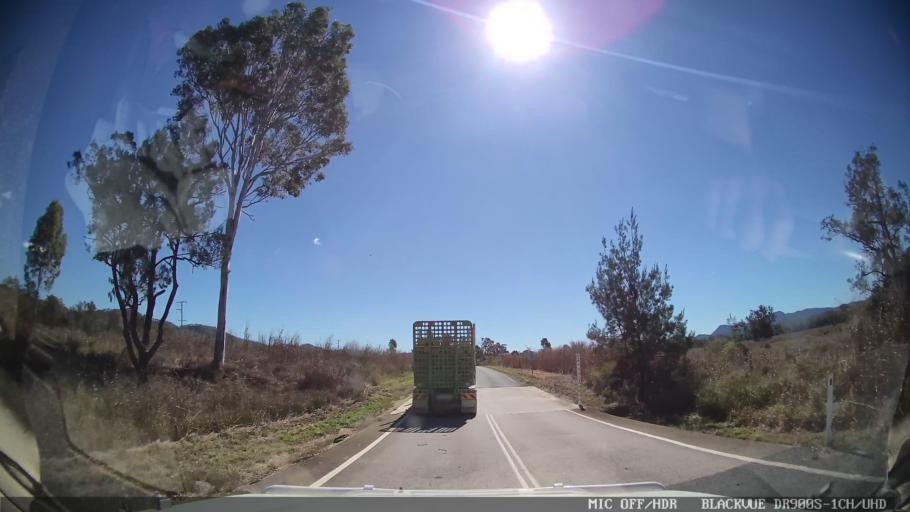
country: AU
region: Queensland
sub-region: Gladstone
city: Toolooa
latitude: -24.2722
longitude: 151.2756
